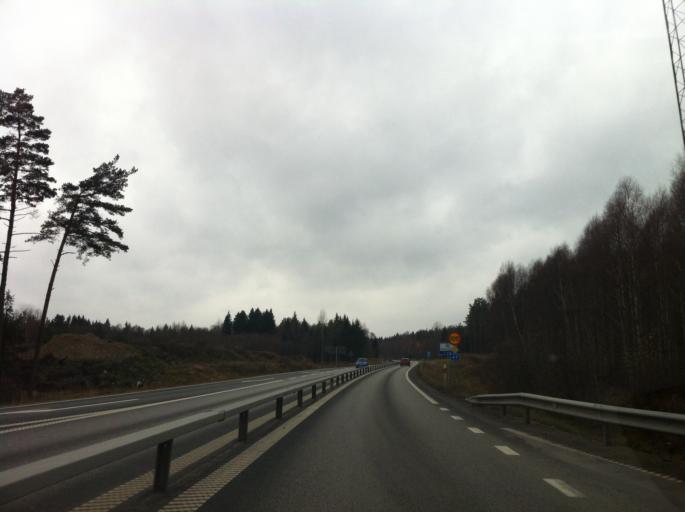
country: SE
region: Joenkoeping
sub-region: Vetlanda Kommun
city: Vetlanda
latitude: 57.4189
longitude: 15.1093
